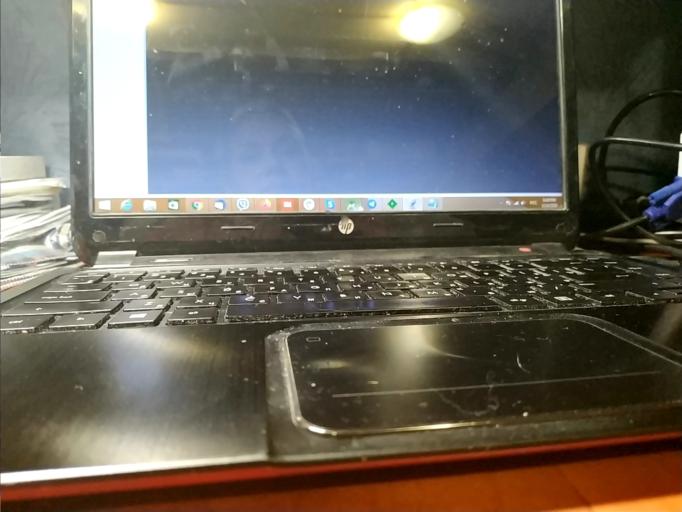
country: RU
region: Arkhangelskaya
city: Onega
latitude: 63.5720
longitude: 36.9334
